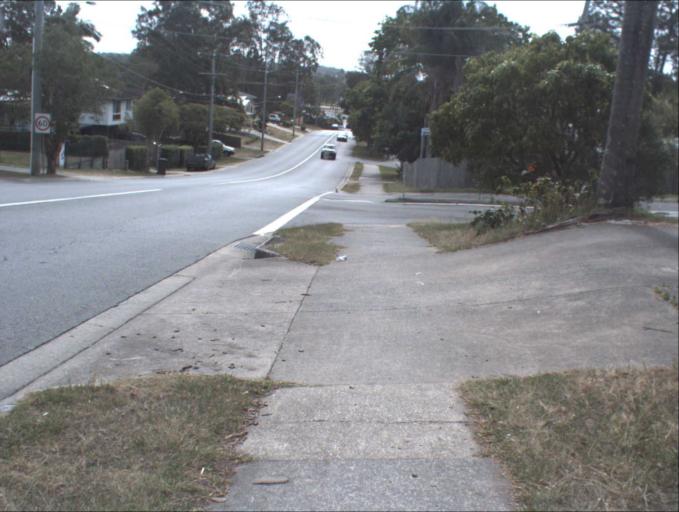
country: AU
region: Queensland
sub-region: Logan
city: Beenleigh
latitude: -27.7081
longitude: 153.1994
